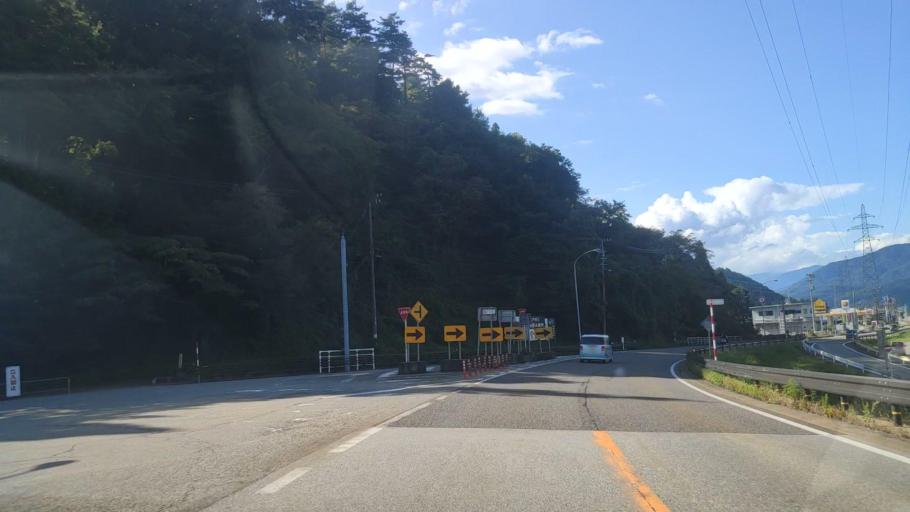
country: JP
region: Gifu
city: Takayama
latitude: 36.2302
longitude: 137.1814
